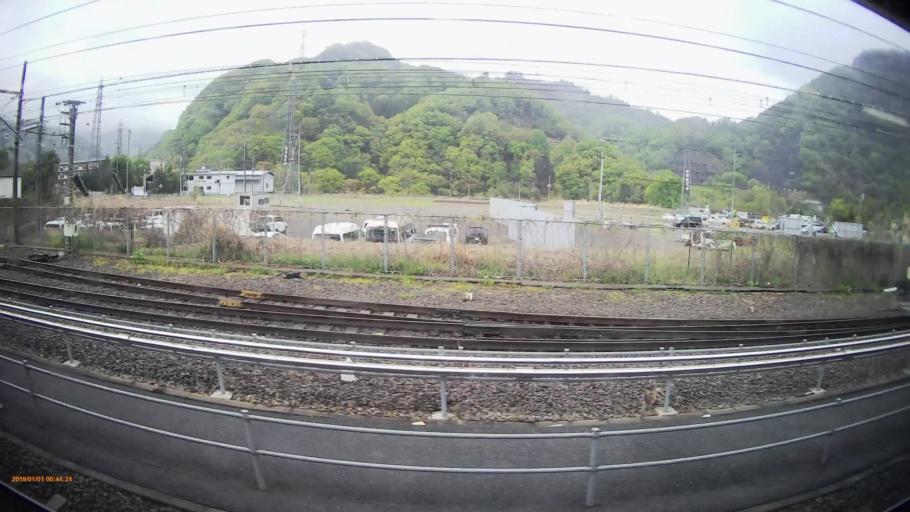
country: JP
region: Yamanashi
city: Otsuki
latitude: 35.6140
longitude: 138.9443
